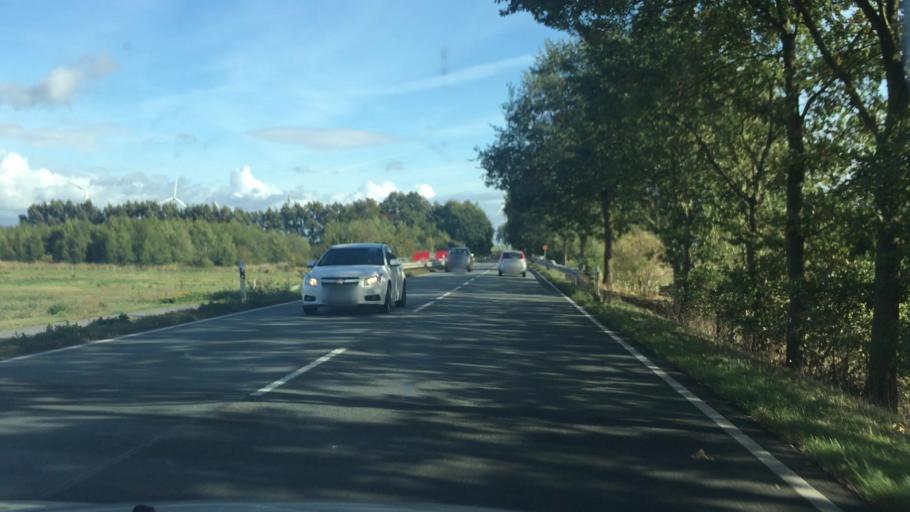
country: DE
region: Lower Saxony
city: Siedenburg
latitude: 52.6751
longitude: 8.9169
